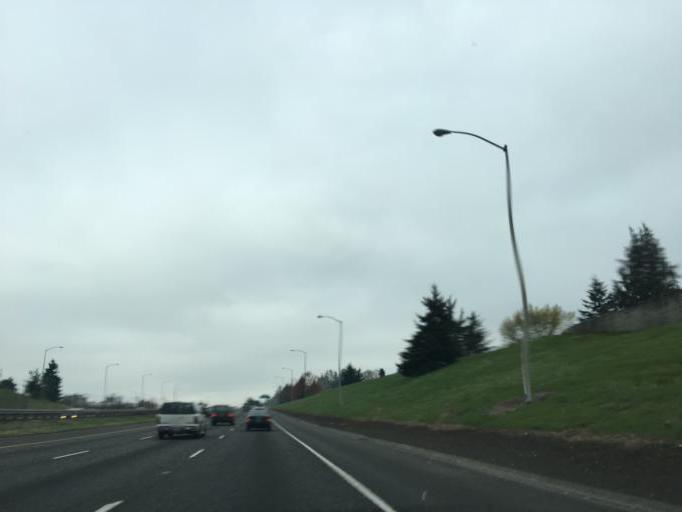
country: US
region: Oregon
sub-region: Multnomah County
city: Lents
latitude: 45.4903
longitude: -122.5656
